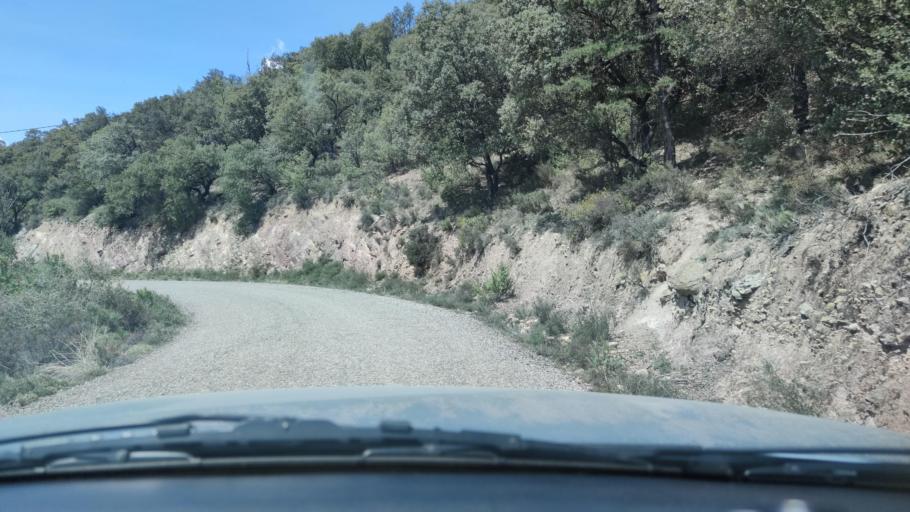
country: ES
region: Catalonia
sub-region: Provincia de Lleida
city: Sort
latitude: 42.3154
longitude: 1.0827
